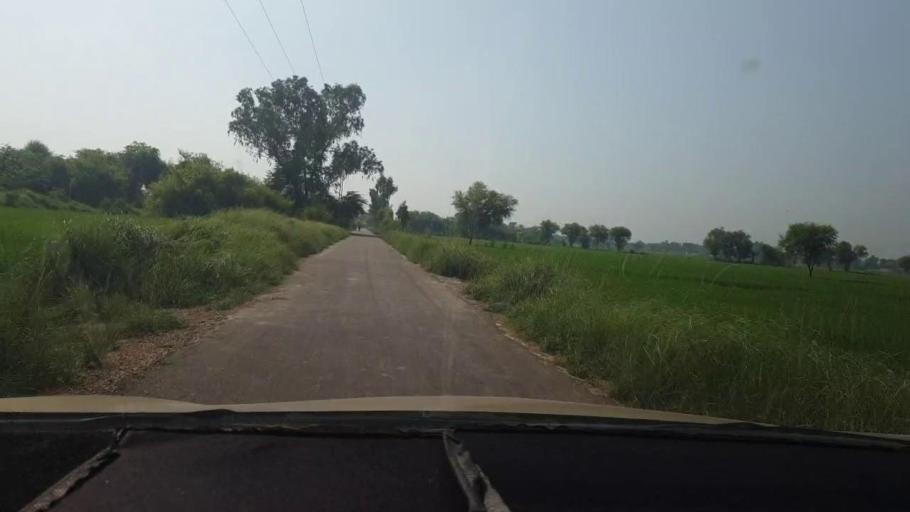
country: PK
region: Sindh
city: Kambar
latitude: 27.5799
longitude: 68.0732
